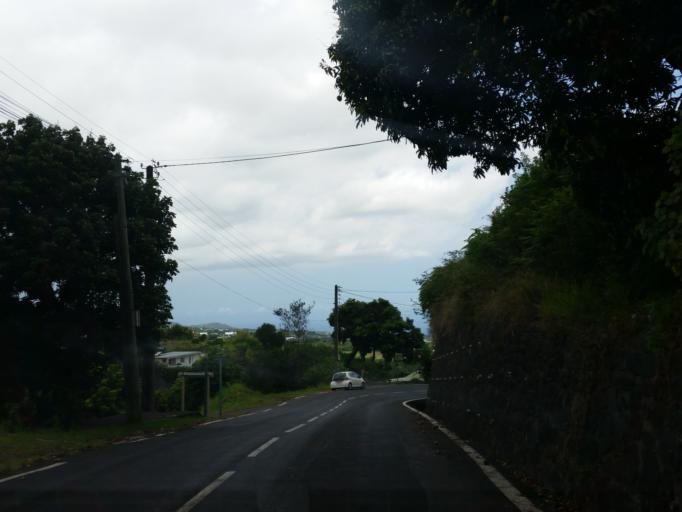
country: RE
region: Reunion
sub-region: Reunion
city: L'Entre-Deux
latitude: -21.2471
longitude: 55.4795
